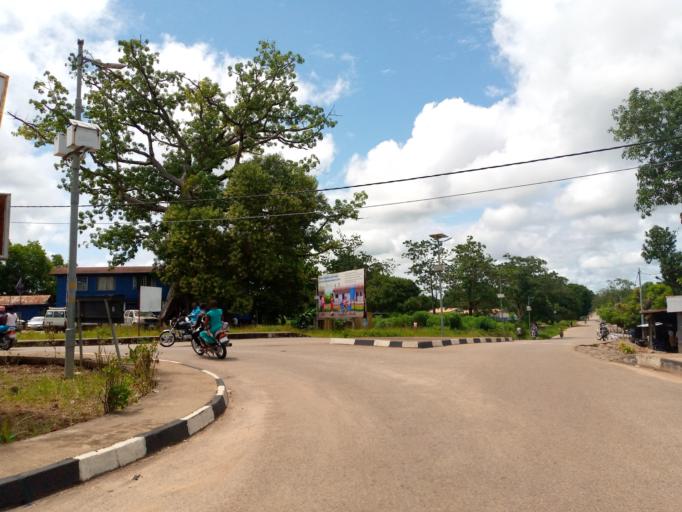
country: SL
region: Northern Province
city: Magburaka
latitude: 8.7196
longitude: -11.9389
